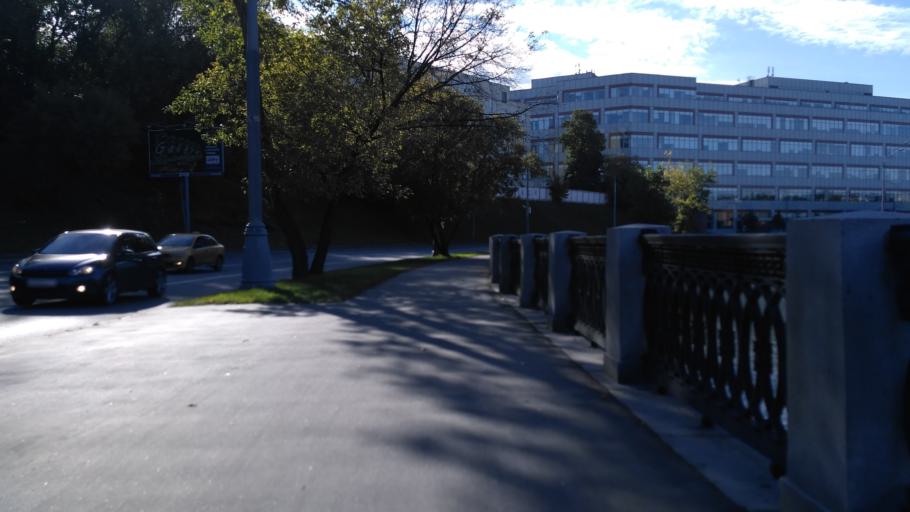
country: RU
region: Moskovskaya
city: Bogorodskoye
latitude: 55.7937
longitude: 37.7054
